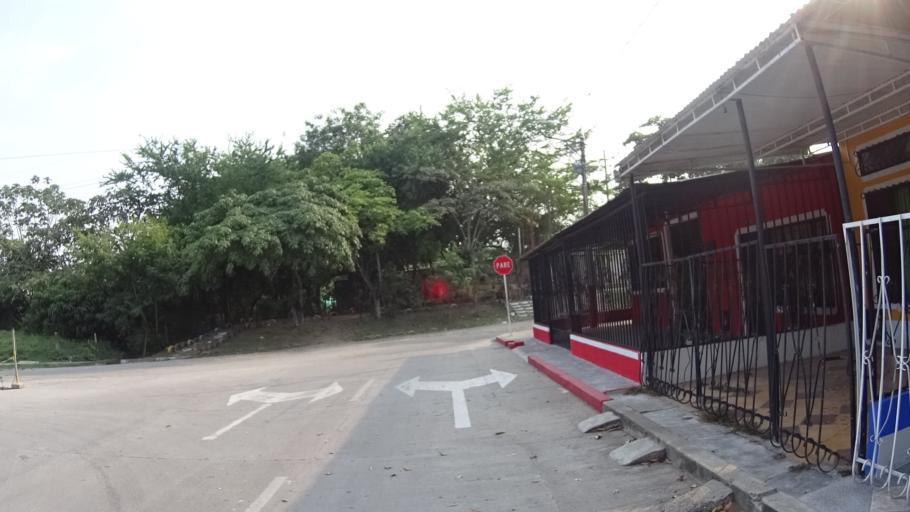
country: CO
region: Cundinamarca
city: Puerto Salgar
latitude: 5.4742
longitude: -74.6779
